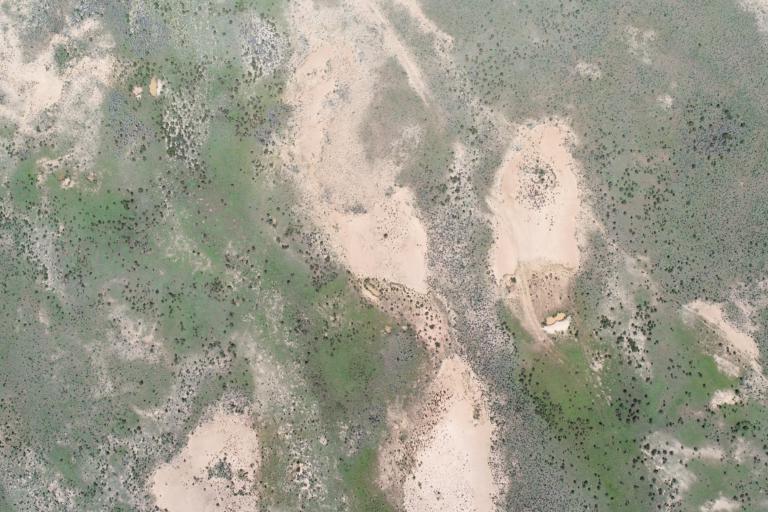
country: BO
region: La Paz
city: Curahuara de Carangas
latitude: -17.2956
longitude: -68.5219
